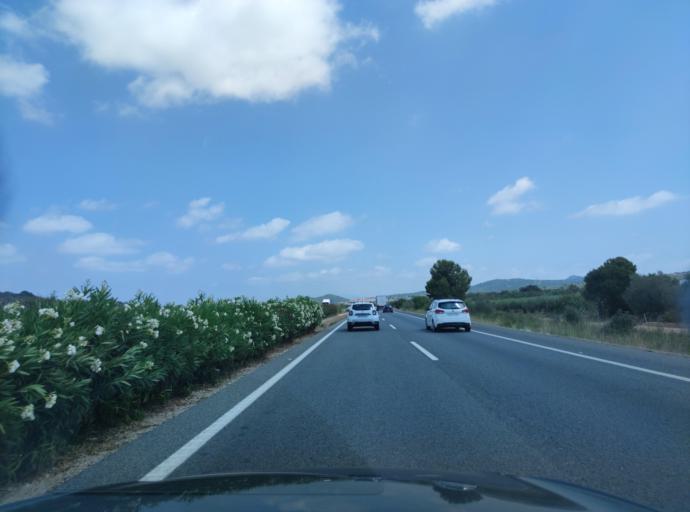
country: ES
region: Catalonia
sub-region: Provincia de Tarragona
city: Santa Barbara
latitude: 40.6467
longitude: 0.5055
